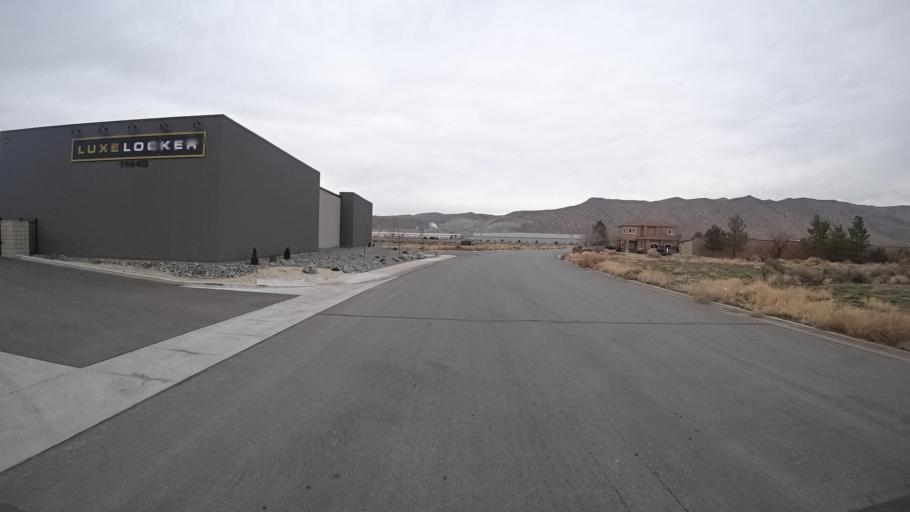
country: US
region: Nevada
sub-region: Washoe County
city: Spanish Springs
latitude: 39.6775
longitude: -119.7021
